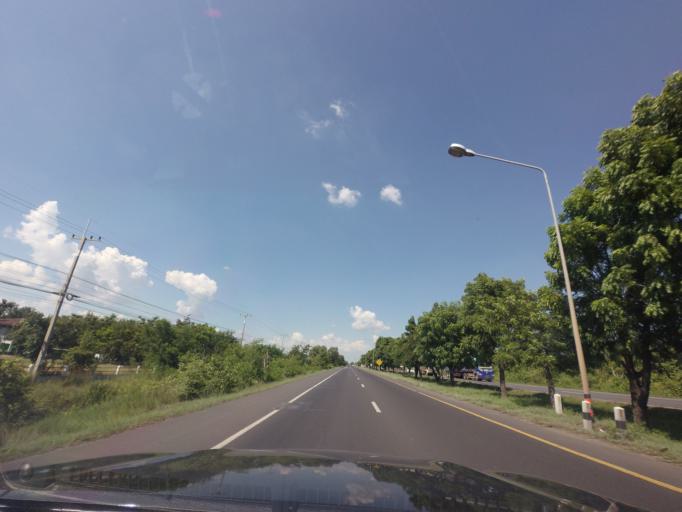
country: TH
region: Nakhon Ratchasima
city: Non Sung
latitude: 15.1948
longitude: 102.3491
